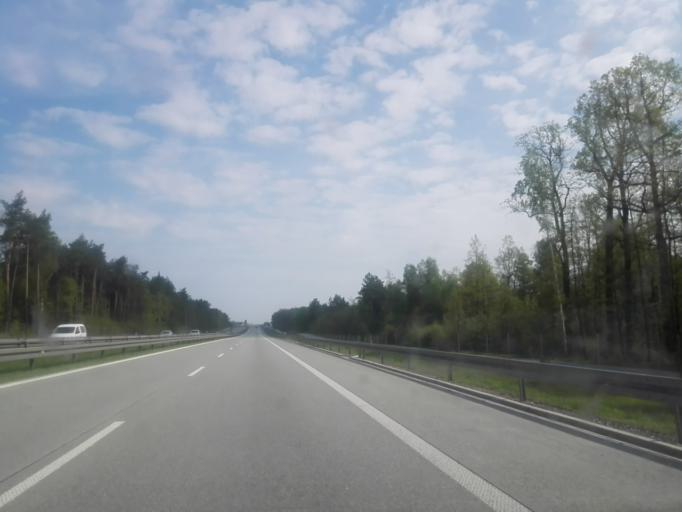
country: PL
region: Lodz Voivodeship
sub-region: Powiat rawski
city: Rawa Mazowiecka
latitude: 51.7246
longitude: 20.2254
